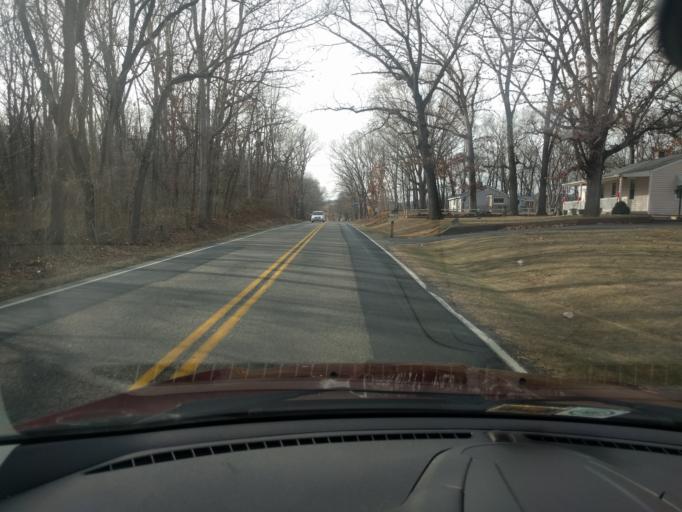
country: US
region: Virginia
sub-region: Augusta County
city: Stuarts Draft
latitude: 38.0434
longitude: -79.0981
